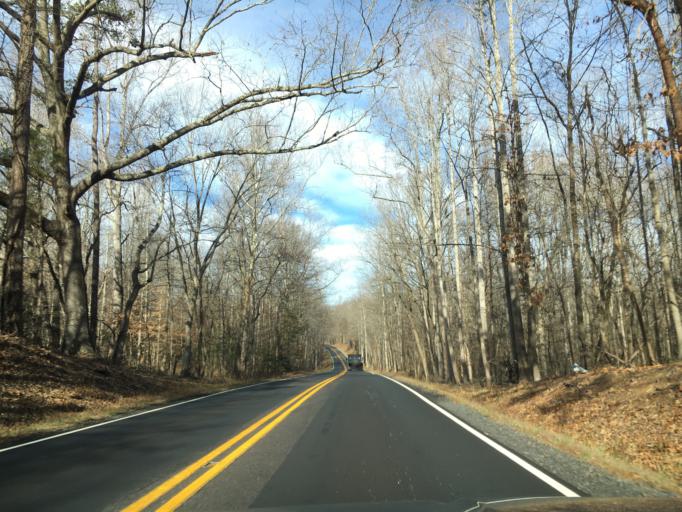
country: US
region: Virginia
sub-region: Louisa County
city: Louisa
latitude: 38.1492
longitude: -77.9264
